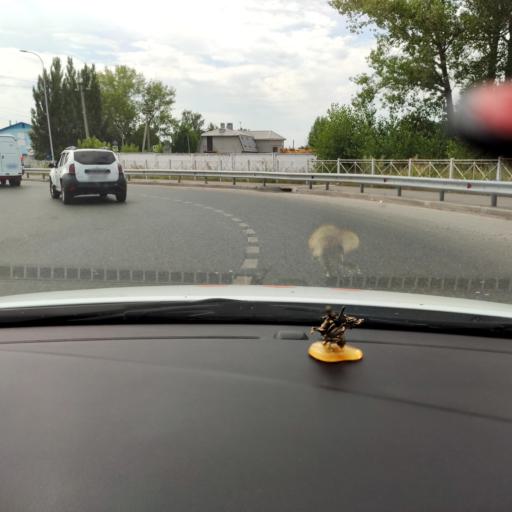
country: RU
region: Tatarstan
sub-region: Zelenodol'skiy Rayon
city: Zelenodolsk
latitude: 55.8403
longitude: 48.5404
